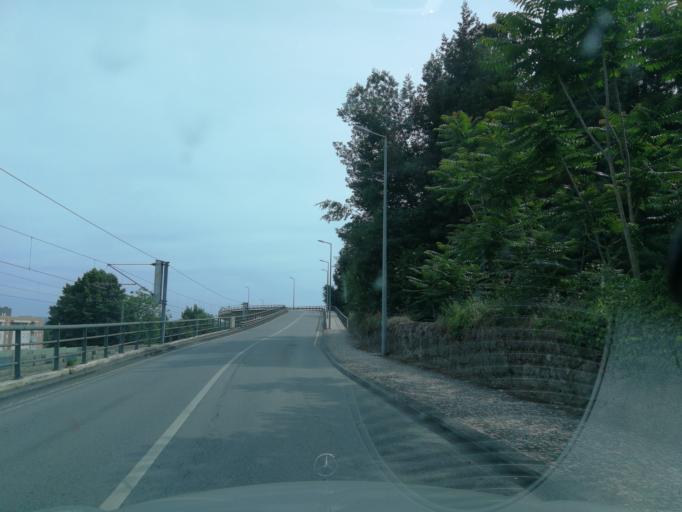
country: PT
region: Braga
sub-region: Vila Nova de Famalicao
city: Vila Nova de Famalicao
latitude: 41.4120
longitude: -8.5267
